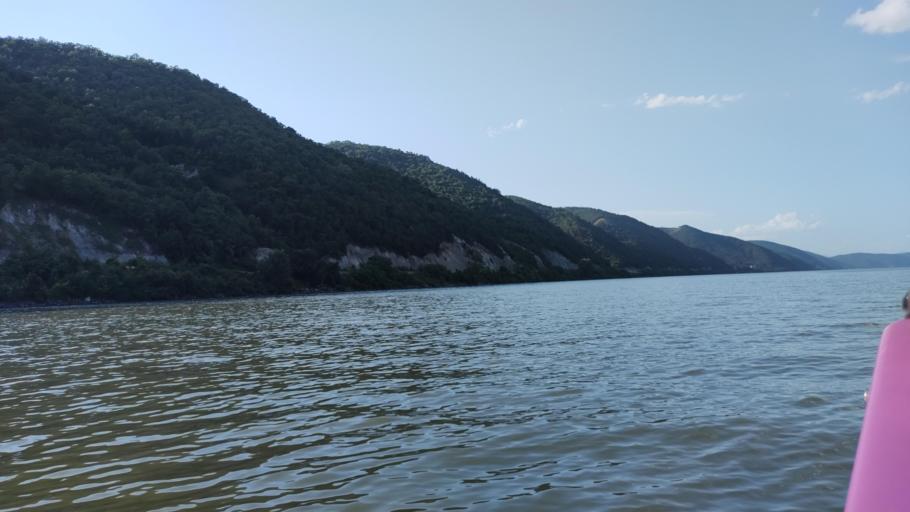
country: RO
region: Mehedinti
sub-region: Comuna Svinita
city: Svinita
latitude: 44.4907
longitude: 22.1856
